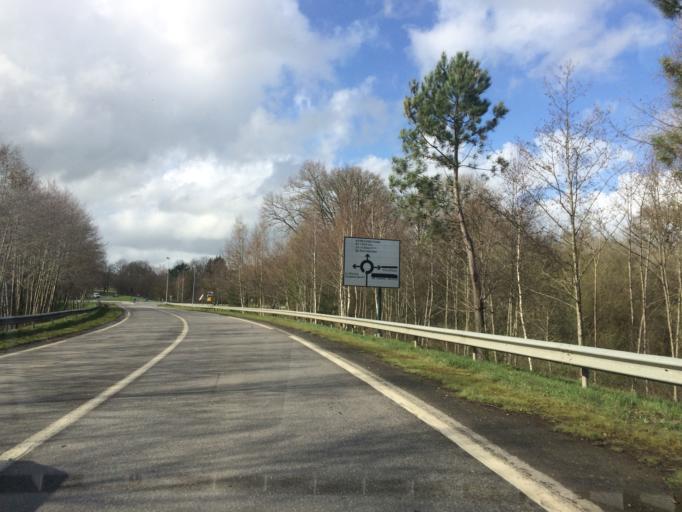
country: FR
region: Brittany
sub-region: Departement du Morbihan
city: La Gacilly
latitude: 47.7718
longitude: -2.1215
